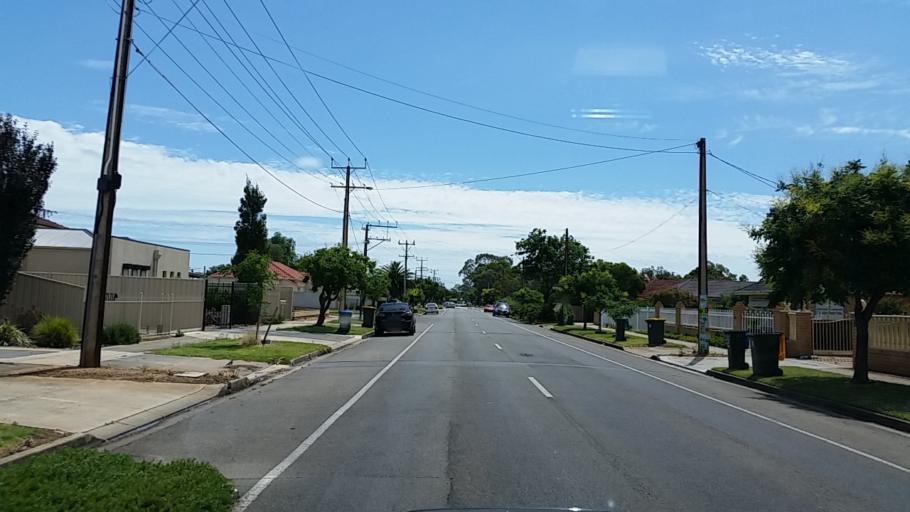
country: AU
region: South Australia
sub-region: Charles Sturt
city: Woodville North
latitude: -34.8640
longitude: 138.5544
